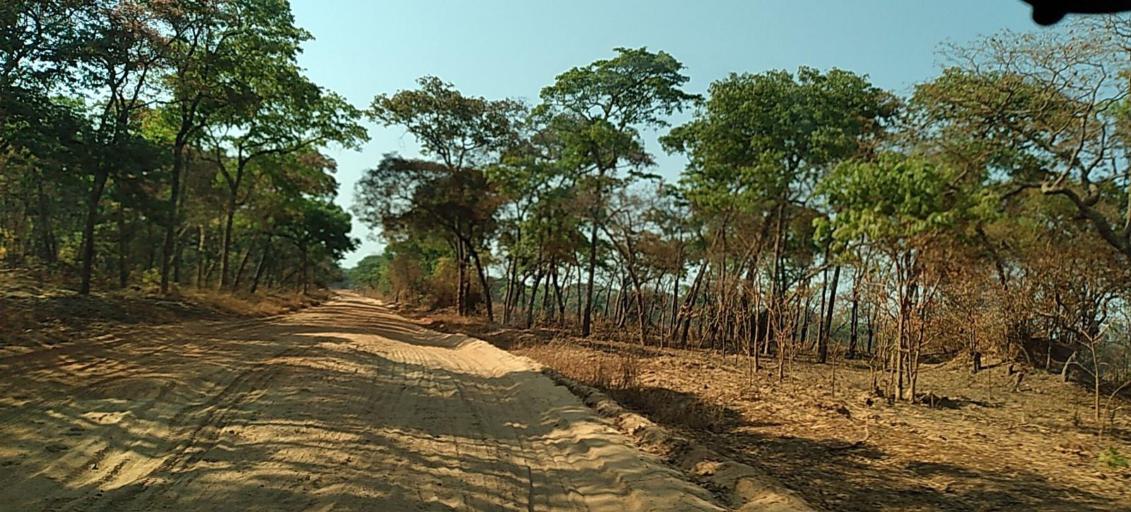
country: ZM
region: North-Western
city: Kasempa
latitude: -13.6812
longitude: 26.0239
